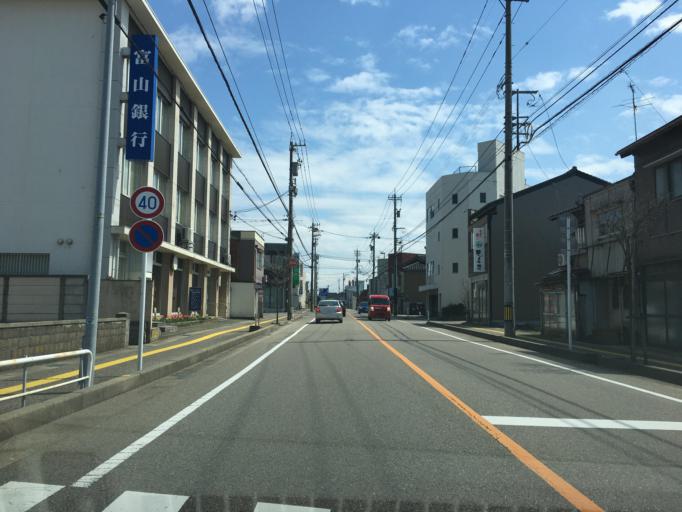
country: JP
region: Toyama
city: Nishishinminato
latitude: 36.7801
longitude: 137.0845
